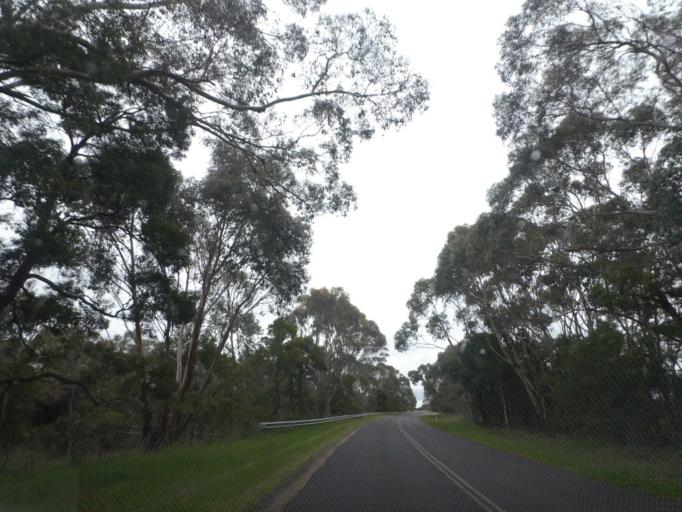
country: AU
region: Victoria
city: Brown Hill
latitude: -37.5960
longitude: 144.1592
